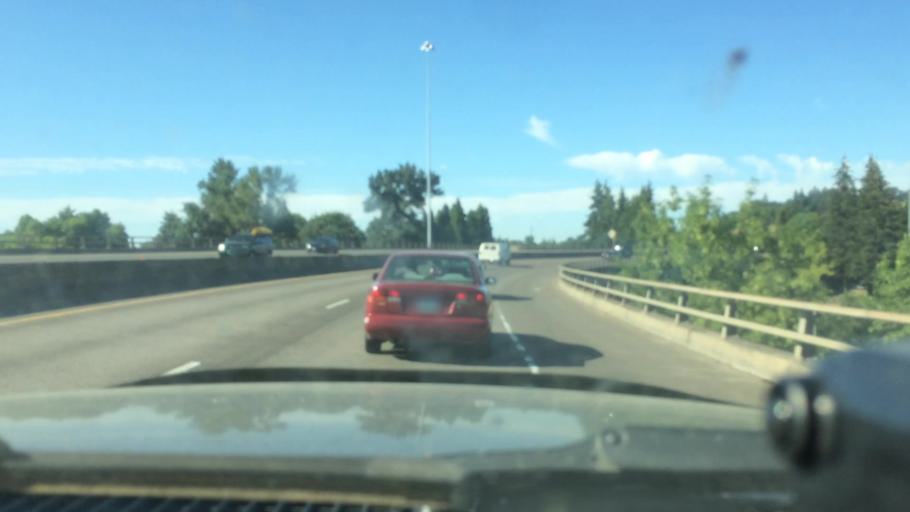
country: US
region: Oregon
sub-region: Lane County
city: Eugene
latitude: 44.0631
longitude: -123.1010
